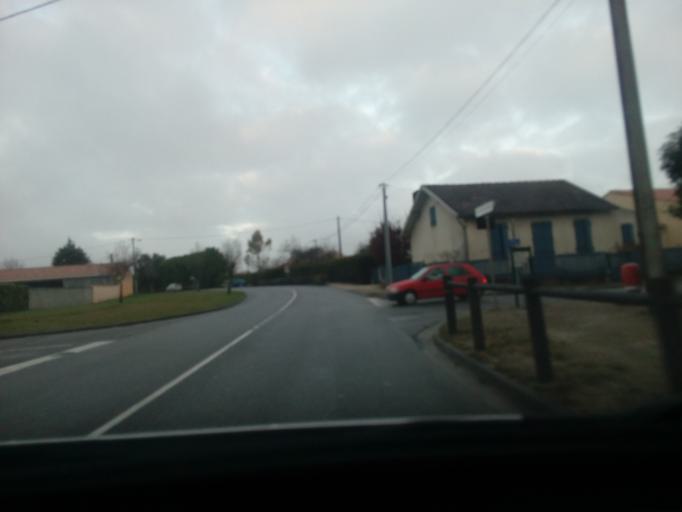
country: FR
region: Poitou-Charentes
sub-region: Departement de la Charente
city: Barbezieux-Saint-Hilaire
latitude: 45.4786
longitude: -0.1521
